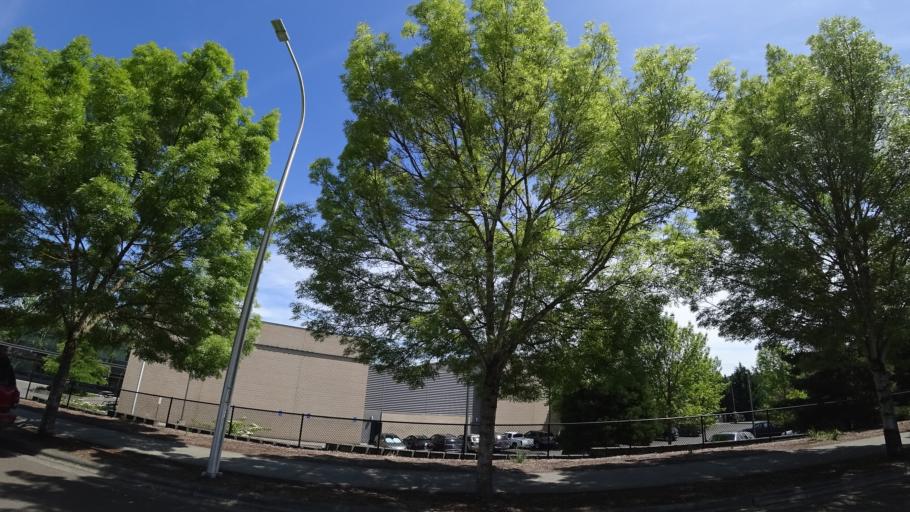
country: US
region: Oregon
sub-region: Washington County
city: Aloha
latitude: 45.4834
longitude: -122.8547
